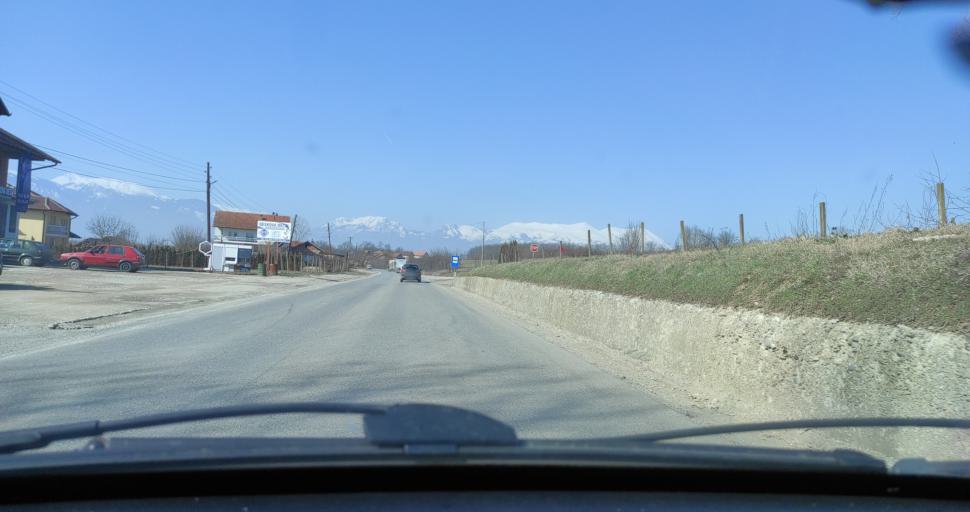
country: XK
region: Pec
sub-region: Komuna e Pejes
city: Kosuriq
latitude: 42.6219
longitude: 20.4750
